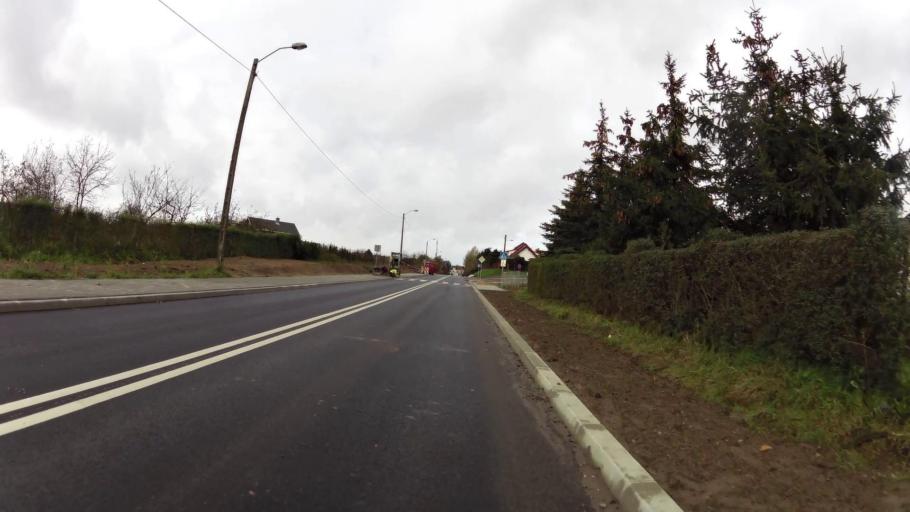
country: PL
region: West Pomeranian Voivodeship
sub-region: Powiat gryfinski
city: Gryfino
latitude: 53.2451
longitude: 14.5008
